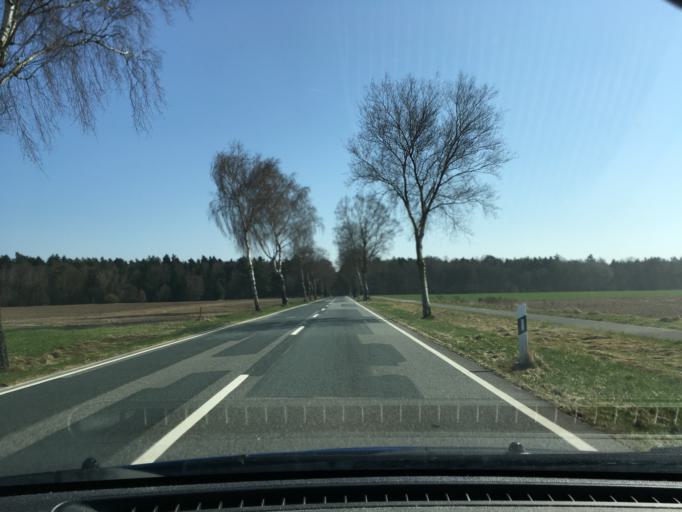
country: DE
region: Lower Saxony
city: Rehlingen
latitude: 53.0938
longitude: 10.2643
